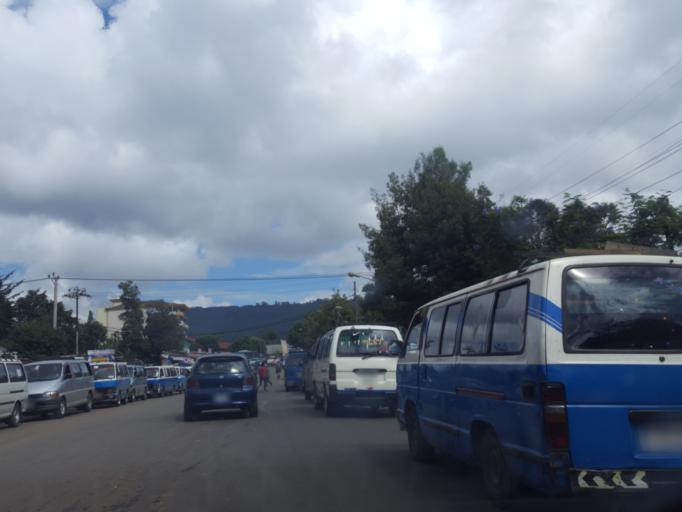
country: ET
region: Adis Abeba
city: Addis Ababa
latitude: 9.0608
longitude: 38.7618
